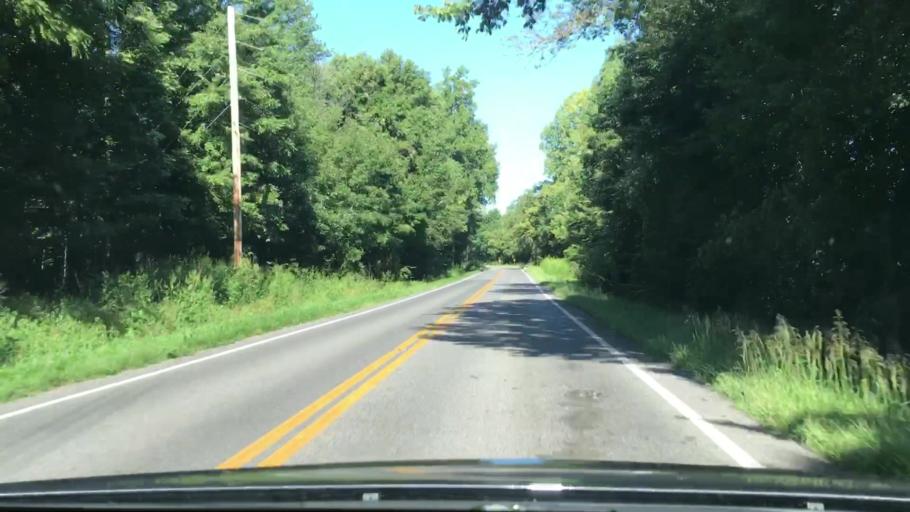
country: US
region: Kentucky
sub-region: Graves County
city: Mayfield
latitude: 36.7813
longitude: -88.5242
